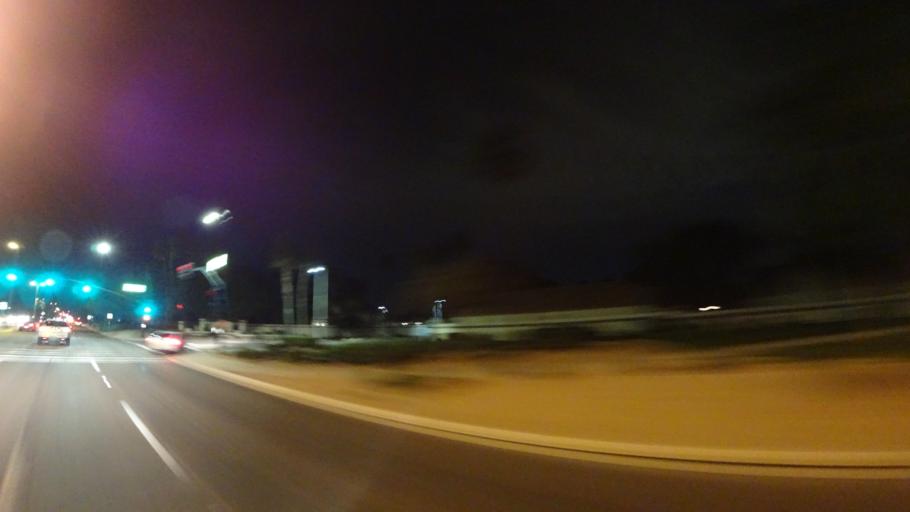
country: US
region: Arizona
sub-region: Maricopa County
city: Gilbert
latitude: 33.3702
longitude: -111.7565
